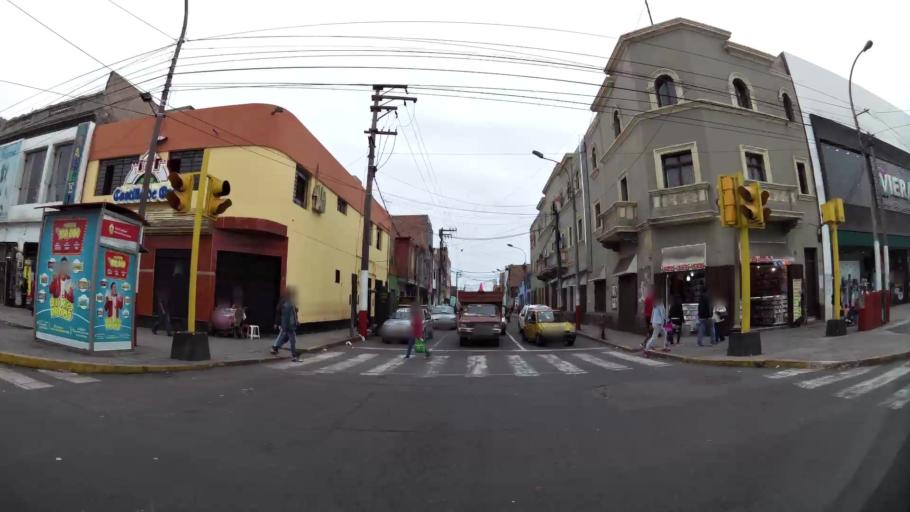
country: PE
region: Callao
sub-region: Callao
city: Callao
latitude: -12.0612
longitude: -77.1416
